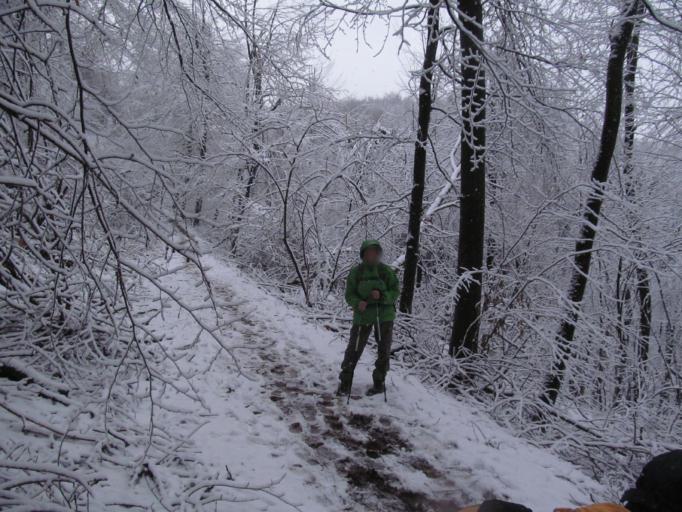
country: HU
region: Nograd
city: Diosjeno
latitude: 47.9466
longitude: 19.0095
